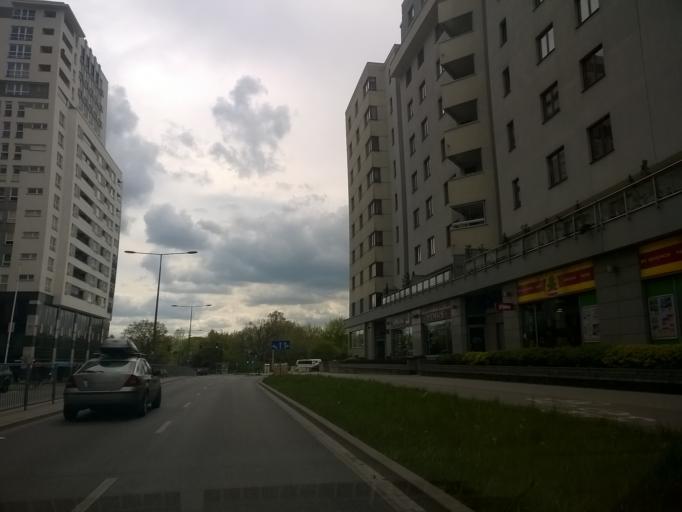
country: PL
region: Masovian Voivodeship
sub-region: Warszawa
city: Mokotow
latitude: 52.1820
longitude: 21.0254
